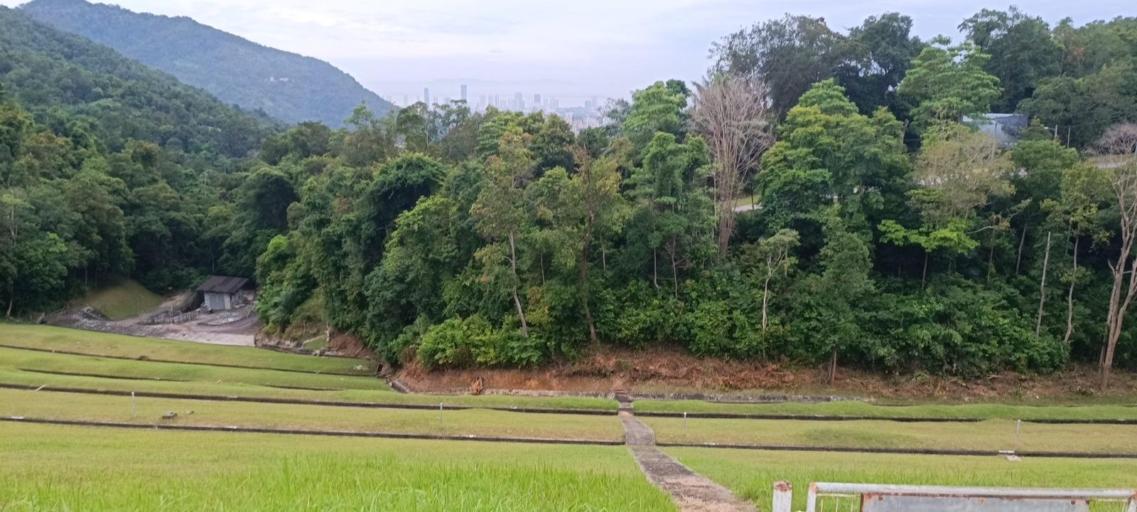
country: MY
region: Penang
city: Kampung Sungai Ara
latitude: 5.3956
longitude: 100.2635
